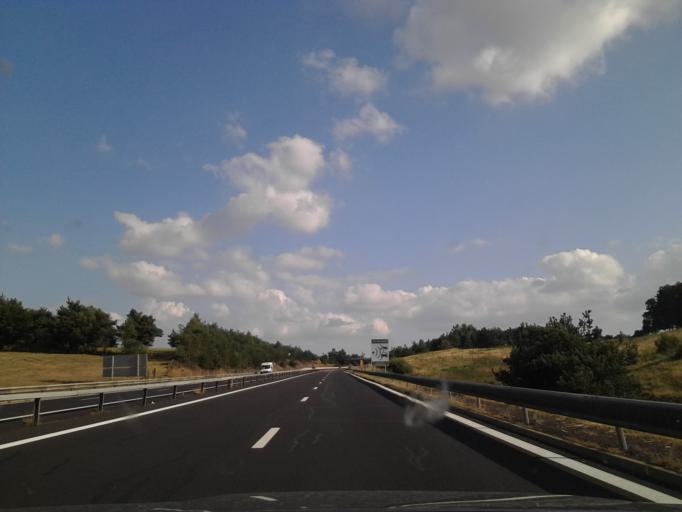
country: FR
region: Auvergne
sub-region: Departement du Cantal
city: Saint-Flour
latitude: 45.1198
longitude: 3.1397
